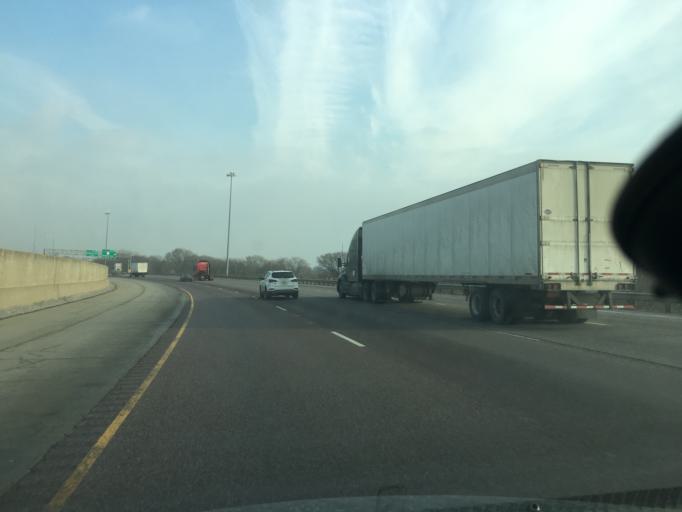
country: US
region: Illinois
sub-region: Cook County
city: Summit
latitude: 41.7963
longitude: -87.8099
